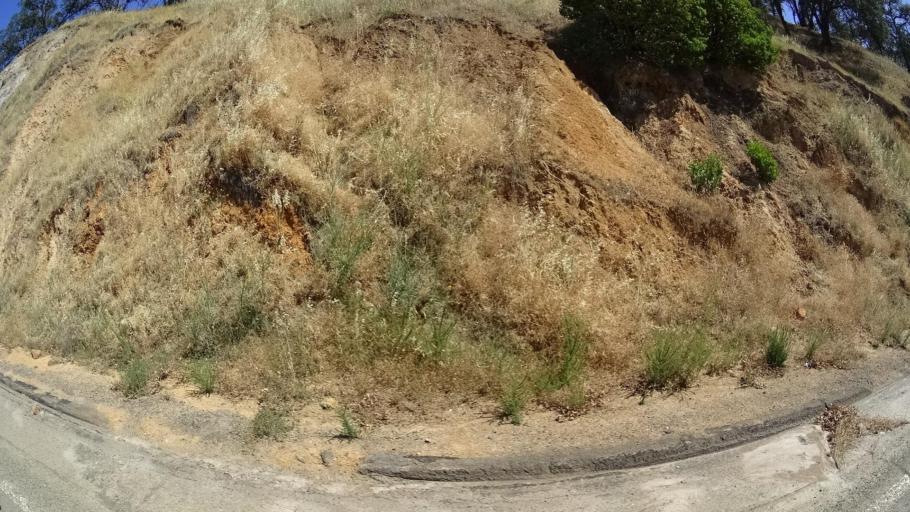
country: US
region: California
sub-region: Lake County
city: Lower Lake
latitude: 38.8895
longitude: -122.5380
